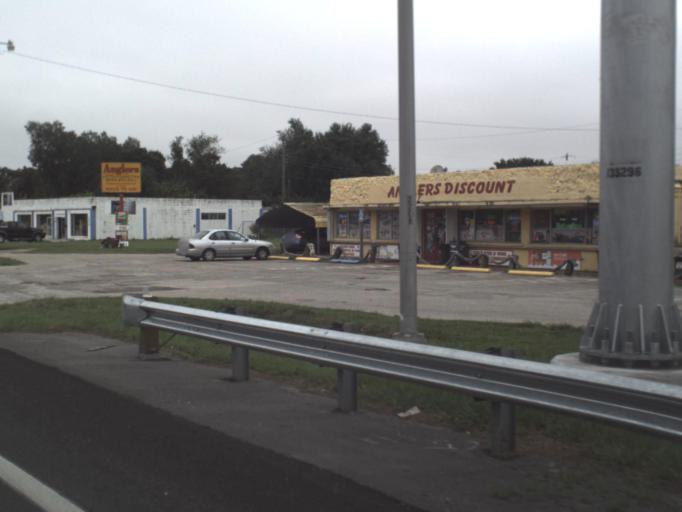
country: US
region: Florida
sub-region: Manatee County
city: Memphis
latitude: 27.5490
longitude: -82.5629
